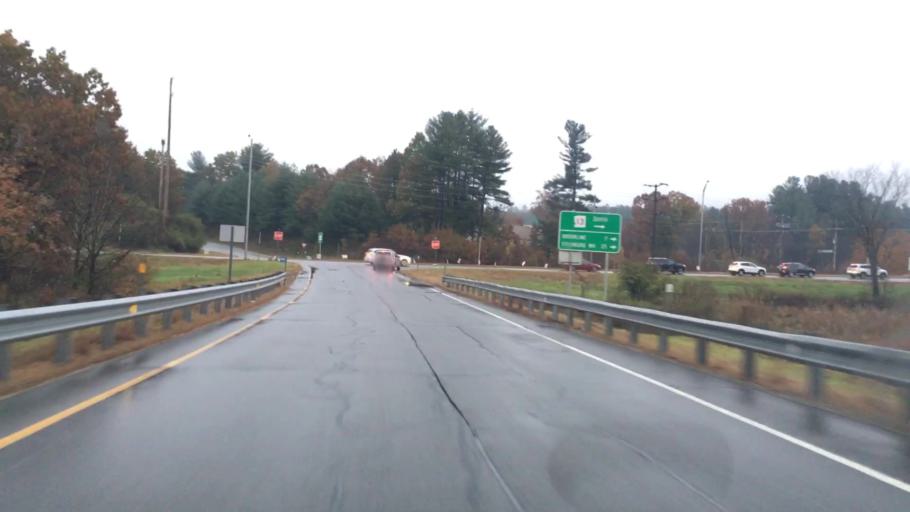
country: US
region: New Hampshire
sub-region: Hillsborough County
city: Milford
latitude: 42.8166
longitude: -71.6474
